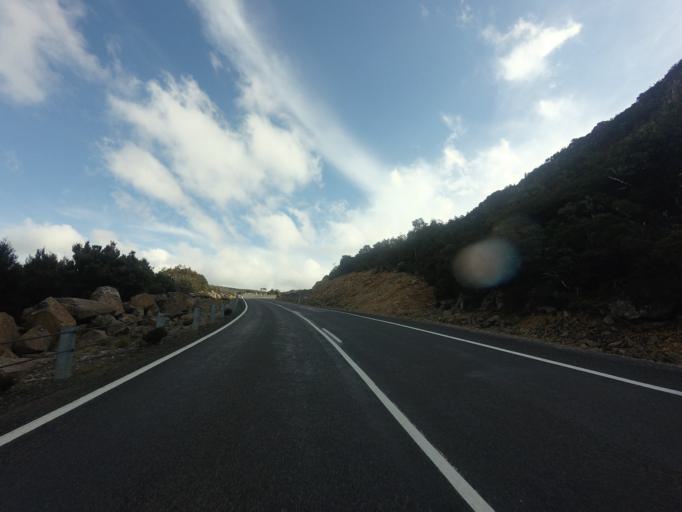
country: AU
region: Tasmania
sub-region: Meander Valley
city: Deloraine
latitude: -41.7301
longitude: 146.7184
